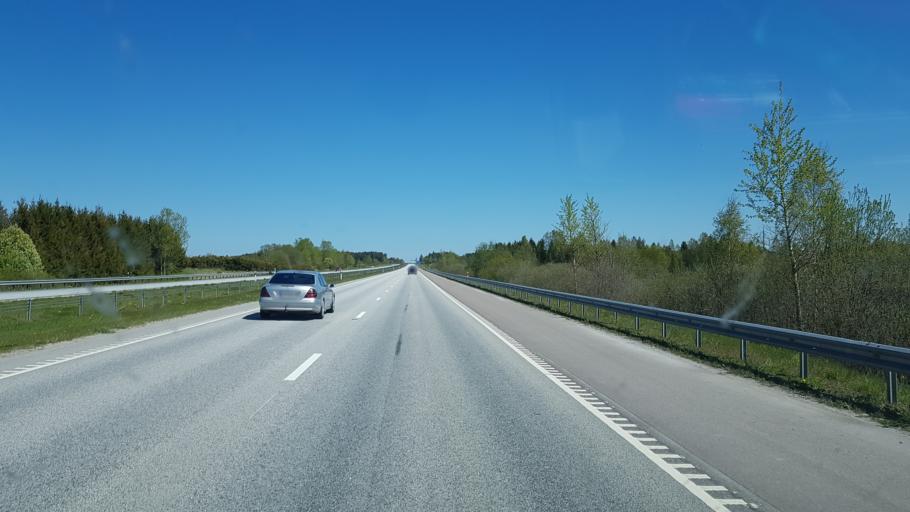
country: EE
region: Harju
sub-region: Kuusalu vald
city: Kuusalu
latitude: 59.4458
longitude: 25.3902
